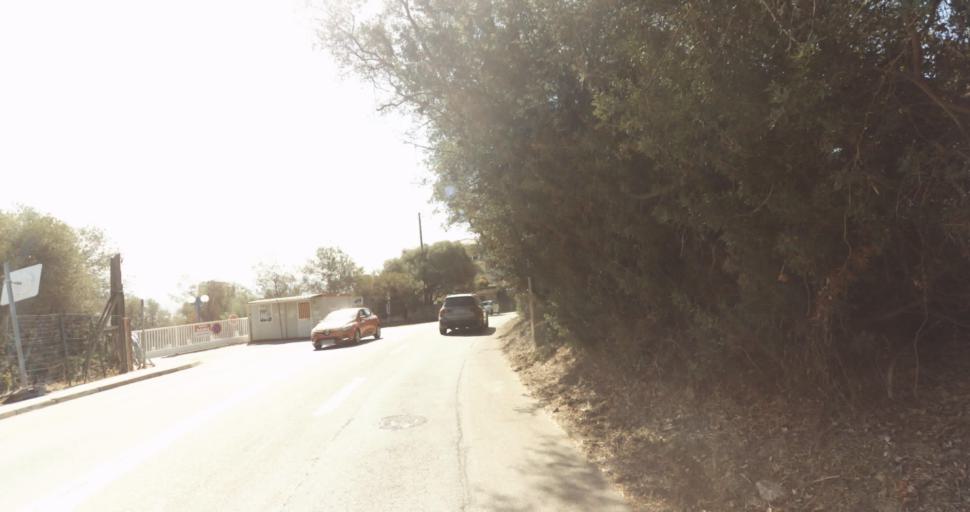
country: FR
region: Corsica
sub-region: Departement de la Corse-du-Sud
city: Ajaccio
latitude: 41.9229
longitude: 8.7307
